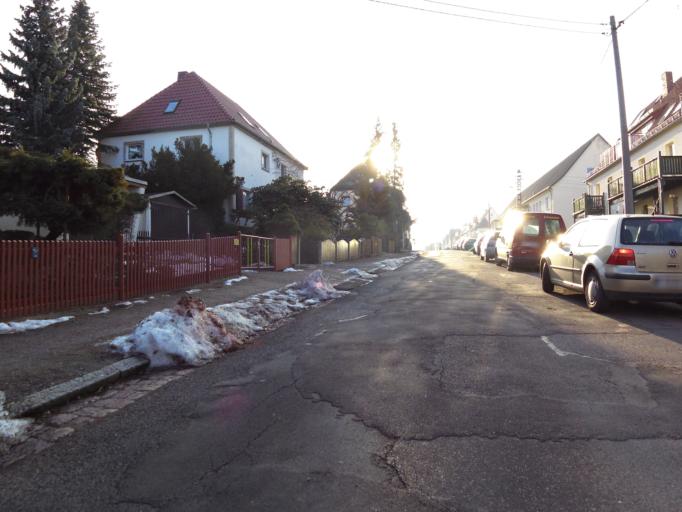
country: DE
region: Saxony
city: Glauchau
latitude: 50.8253
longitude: 12.5554
